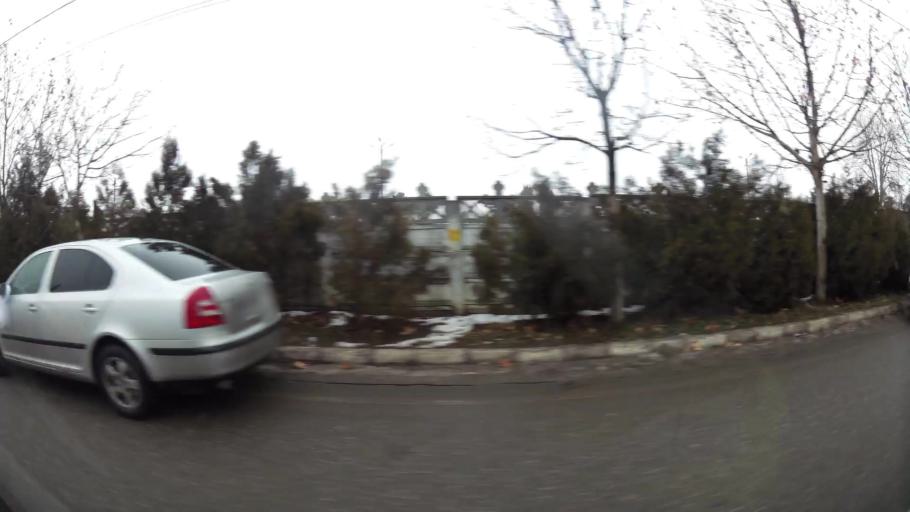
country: RO
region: Ilfov
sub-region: Comuna Chiajna
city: Rosu
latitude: 44.4548
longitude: 26.0082
